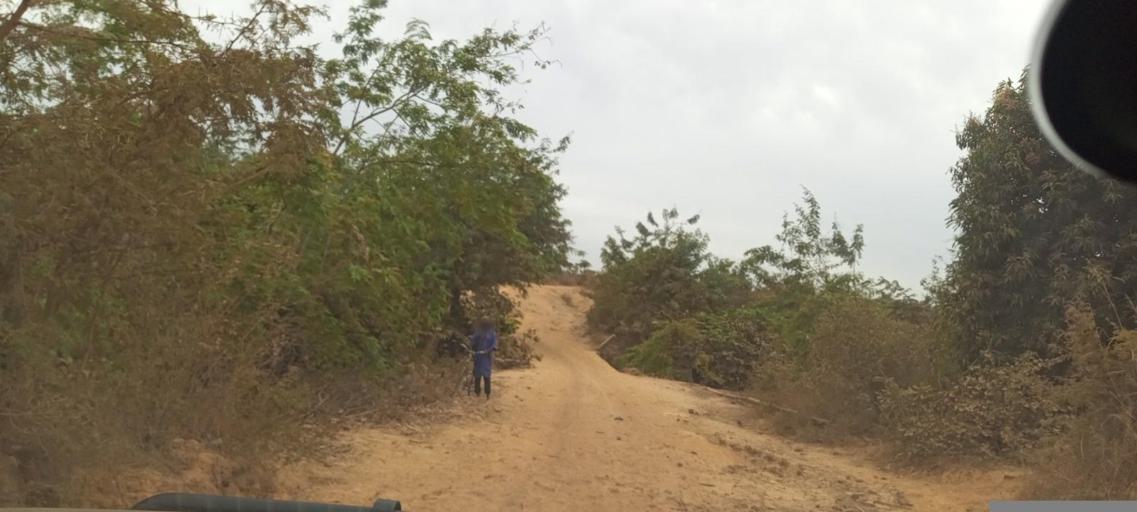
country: ML
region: Koulikoro
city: Kati
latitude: 12.7908
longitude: -8.2555
